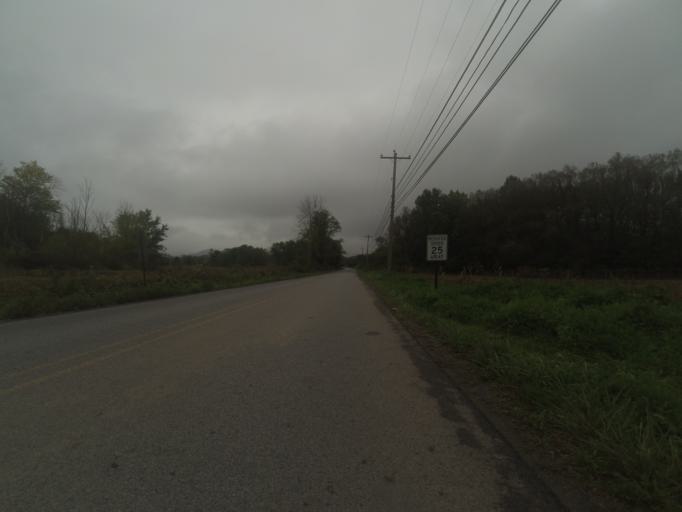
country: US
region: Pennsylvania
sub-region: Huntingdon County
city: McConnellstown
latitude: 40.5498
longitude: -78.0955
